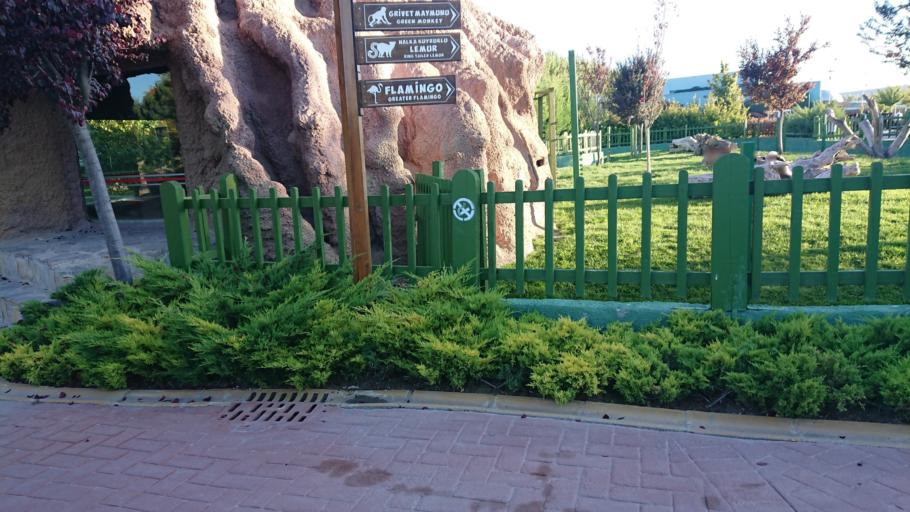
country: TR
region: Eskisehir
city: Eskisehir
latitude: 39.7695
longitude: 30.4752
